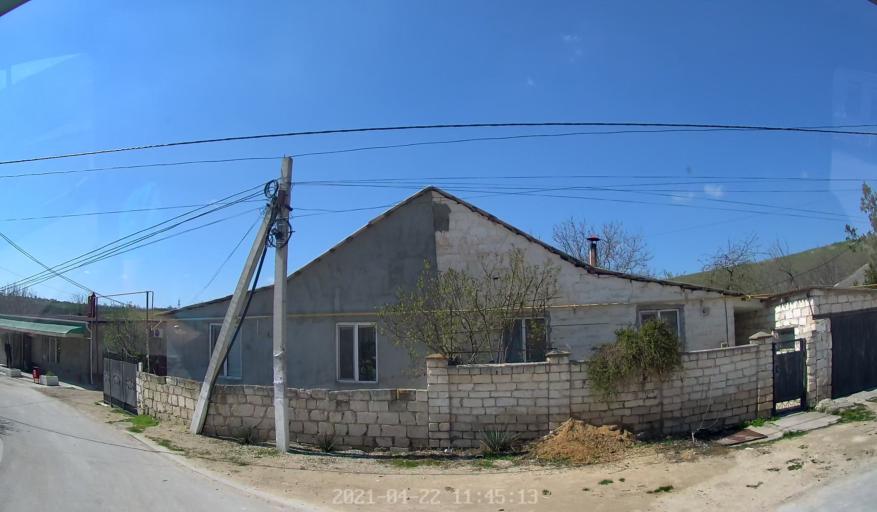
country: MD
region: Chisinau
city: Ciorescu
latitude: 47.1470
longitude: 28.8948
